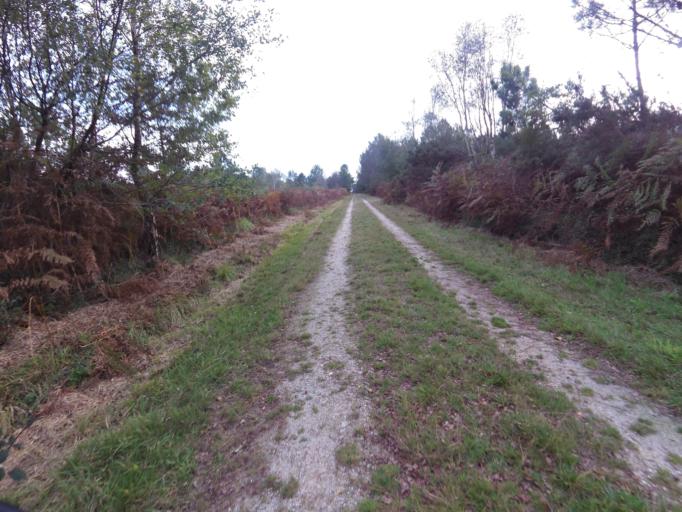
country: FR
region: Brittany
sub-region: Departement du Morbihan
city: Molac
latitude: 47.7556
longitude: -2.4309
